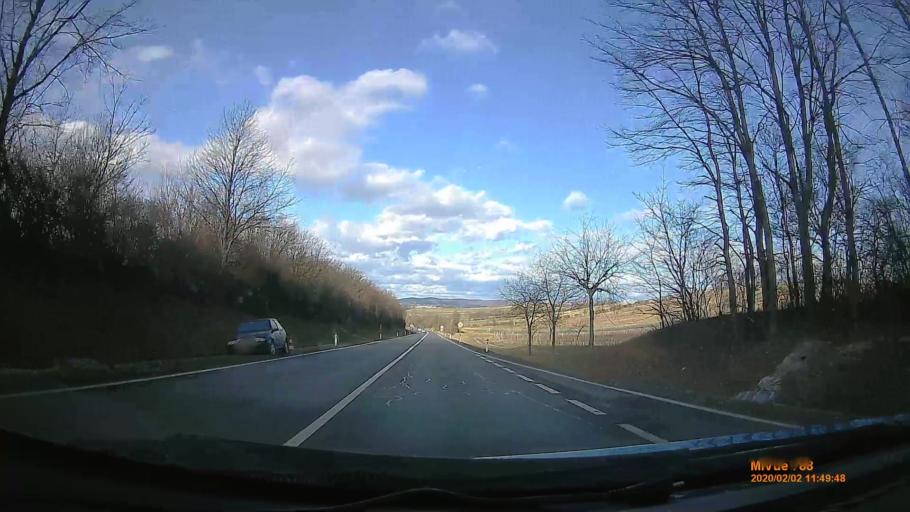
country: AT
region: Burgenland
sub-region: Eisenstadt-Umgebung
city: Klingenbach
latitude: 47.7562
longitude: 16.5463
